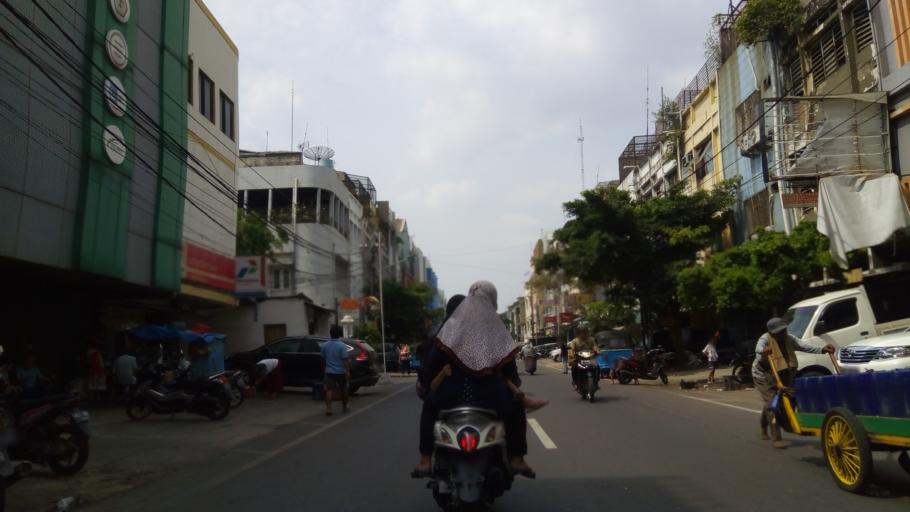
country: ID
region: Jakarta Raya
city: Jakarta
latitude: -6.1593
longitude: 106.8291
